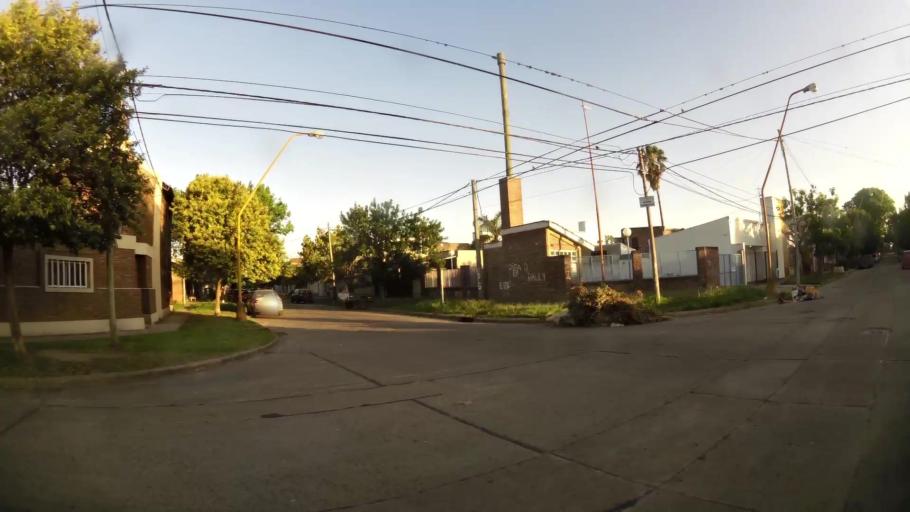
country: AR
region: Santa Fe
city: Santa Fe de la Vera Cruz
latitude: -31.6041
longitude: -60.6869
